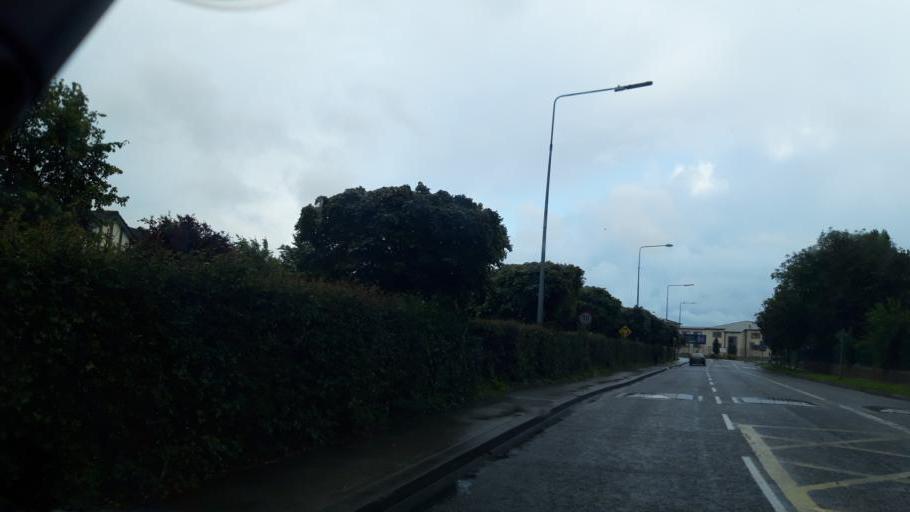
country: IE
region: Leinster
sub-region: Fingal County
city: Blanchardstown
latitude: 53.3714
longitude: -6.3879
